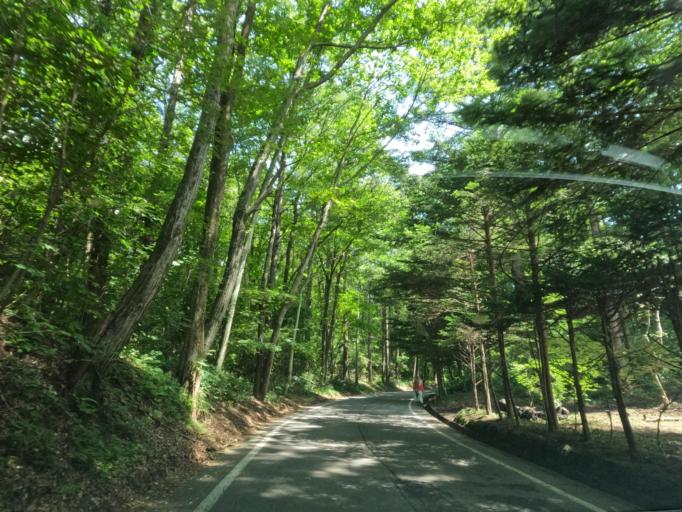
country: JP
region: Nagano
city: Komoro
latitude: 36.3621
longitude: 138.5989
